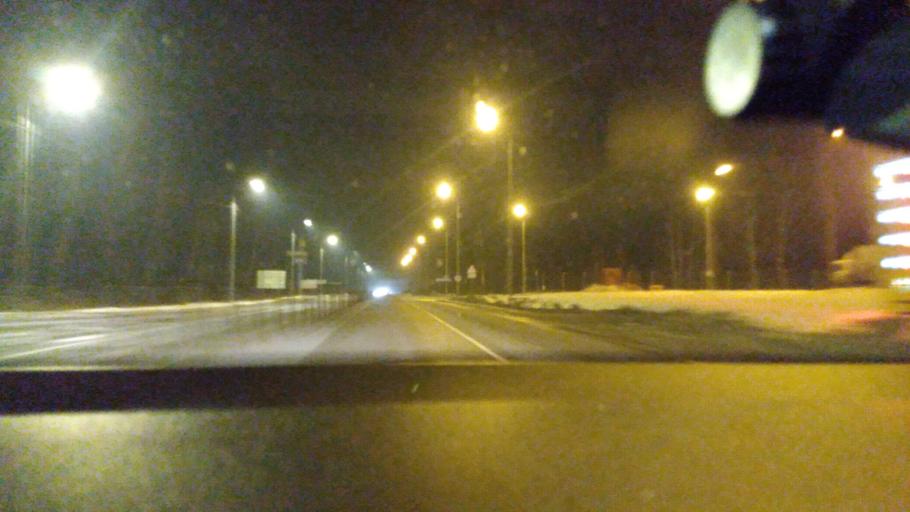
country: RU
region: Moskovskaya
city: Yegor'yevsk
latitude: 55.4176
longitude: 39.0435
